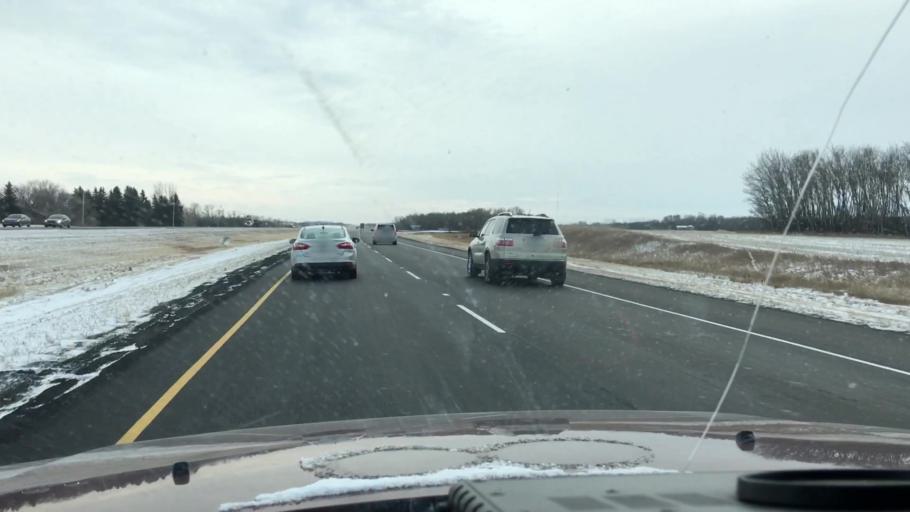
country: CA
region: Saskatchewan
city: Saskatoon
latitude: 52.0163
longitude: -106.5757
